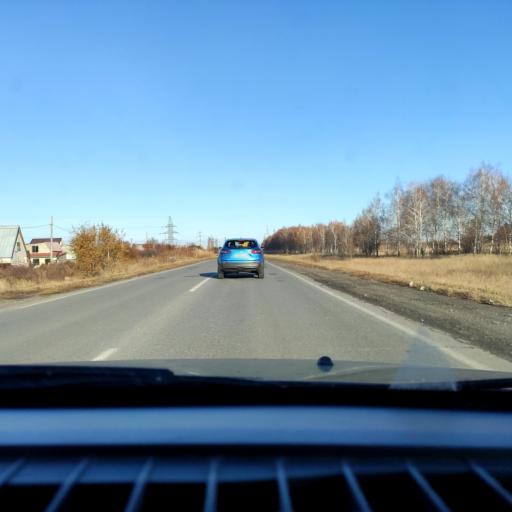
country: RU
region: Samara
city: Tol'yatti
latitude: 53.5804
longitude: 49.3359
